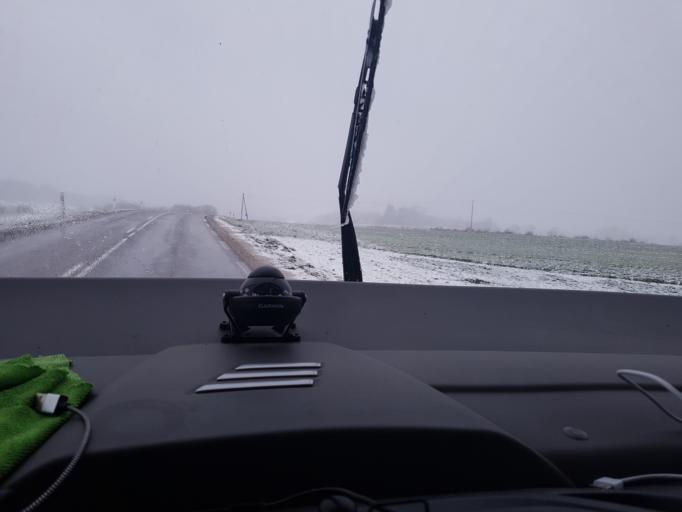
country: FR
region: Lorraine
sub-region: Departement de Meurthe-et-Moselle
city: Baccarat
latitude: 48.4716
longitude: 6.7645
